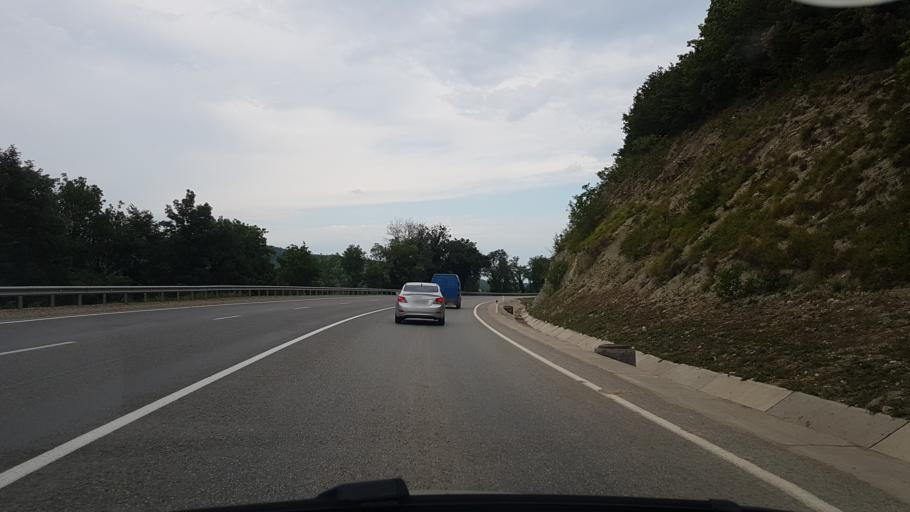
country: RU
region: Krasnodarskiy
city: Dzhubga
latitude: 44.3505
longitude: 38.7069
